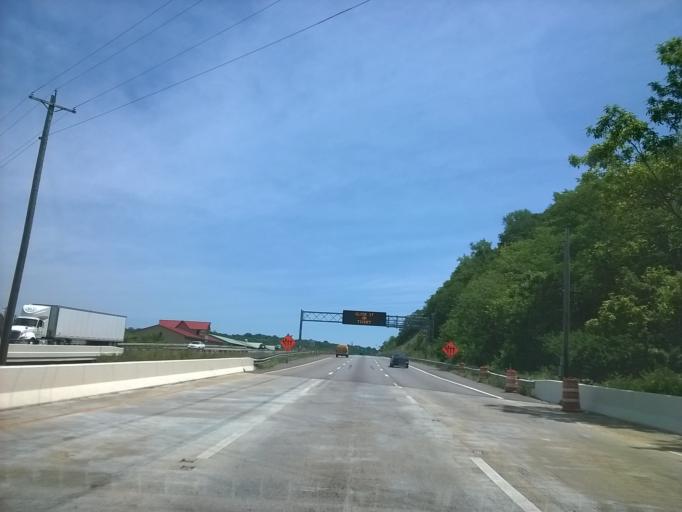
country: US
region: Ohio
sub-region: Hamilton County
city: Miamitown
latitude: 39.2109
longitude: -84.6947
